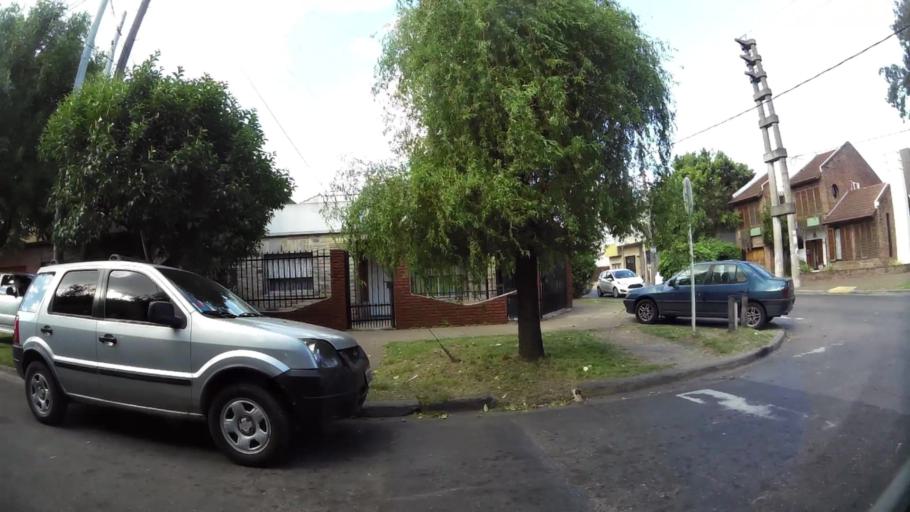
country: AR
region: Buenos Aires
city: San Justo
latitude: -34.6682
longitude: -58.5838
